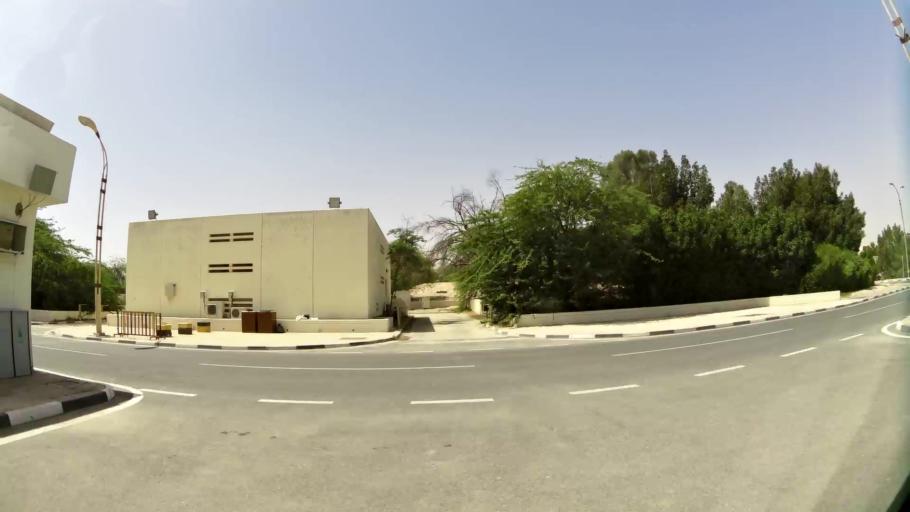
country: QA
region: Baladiyat ad Dawhah
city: Doha
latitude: 25.3689
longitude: 51.4943
